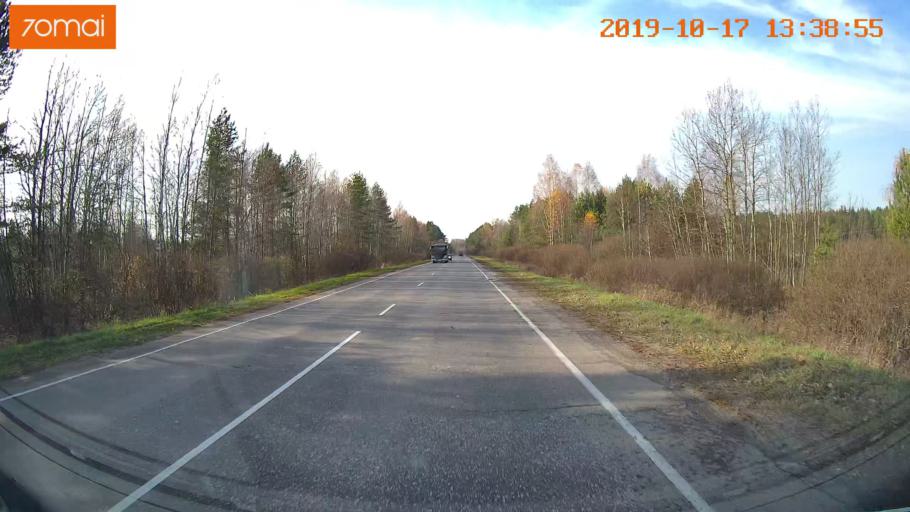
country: RU
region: Rjazan
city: Tuma
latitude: 55.1450
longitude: 40.6011
